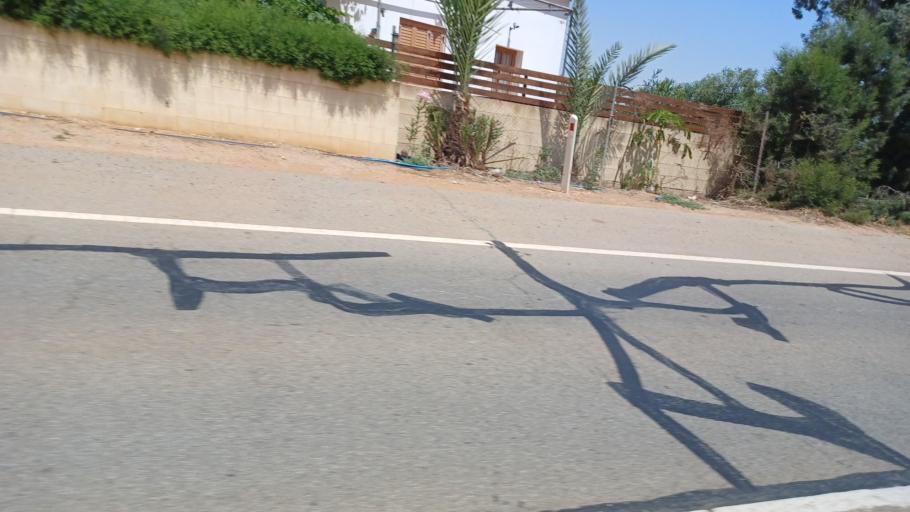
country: CY
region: Ammochostos
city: Liopetri
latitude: 34.9878
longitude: 33.9292
